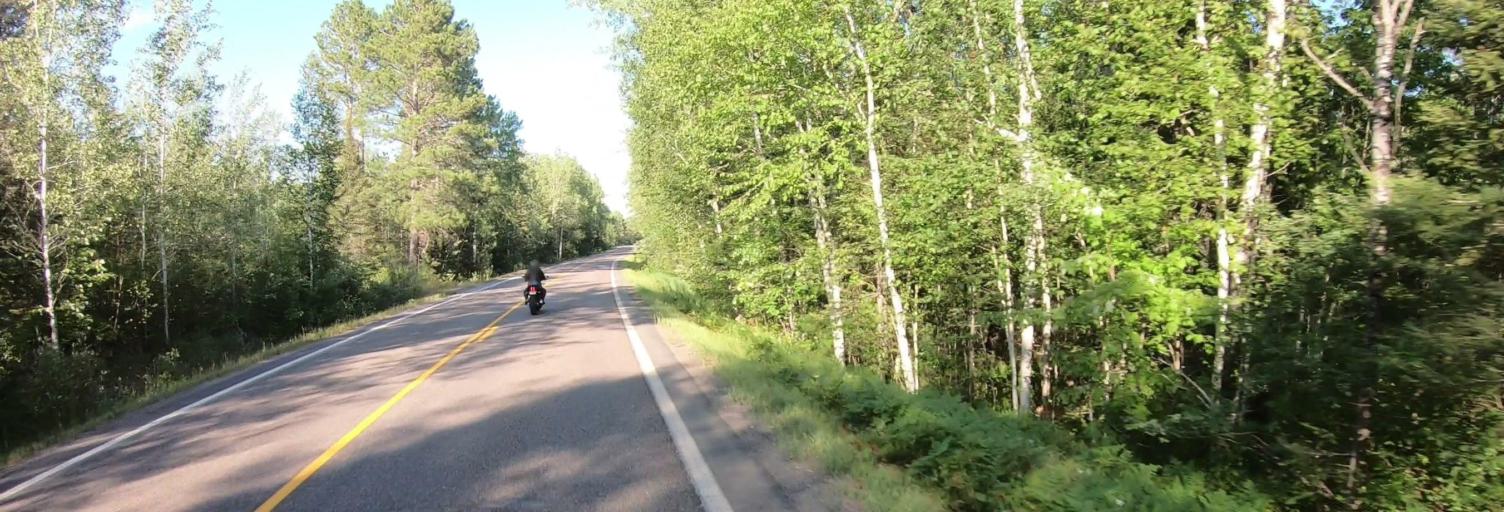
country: US
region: Minnesota
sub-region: Saint Louis County
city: Ely
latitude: 47.9403
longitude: -91.6753
